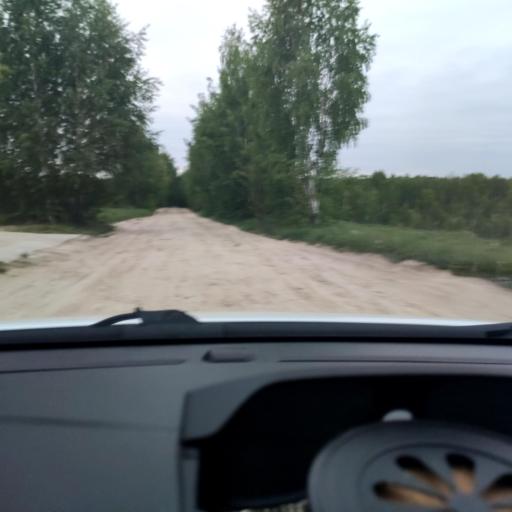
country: RU
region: Tatarstan
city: Vysokaya Gora
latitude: 55.8568
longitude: 49.2508
